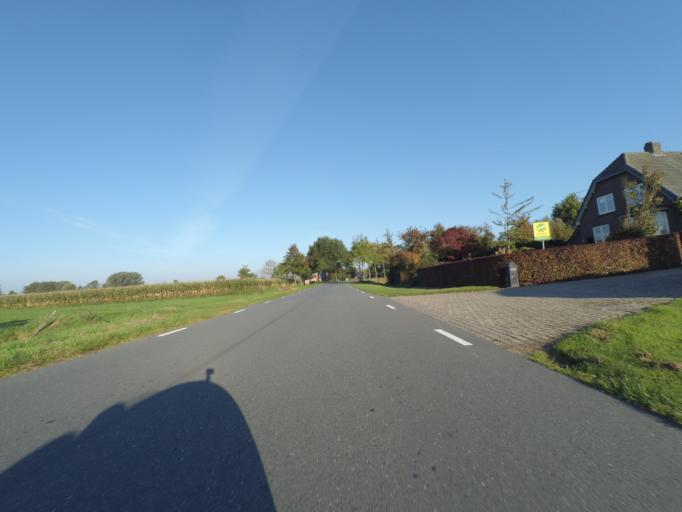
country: NL
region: Gelderland
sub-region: Gemeente Barneveld
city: Zwartebroek
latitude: 52.1864
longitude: 5.5203
